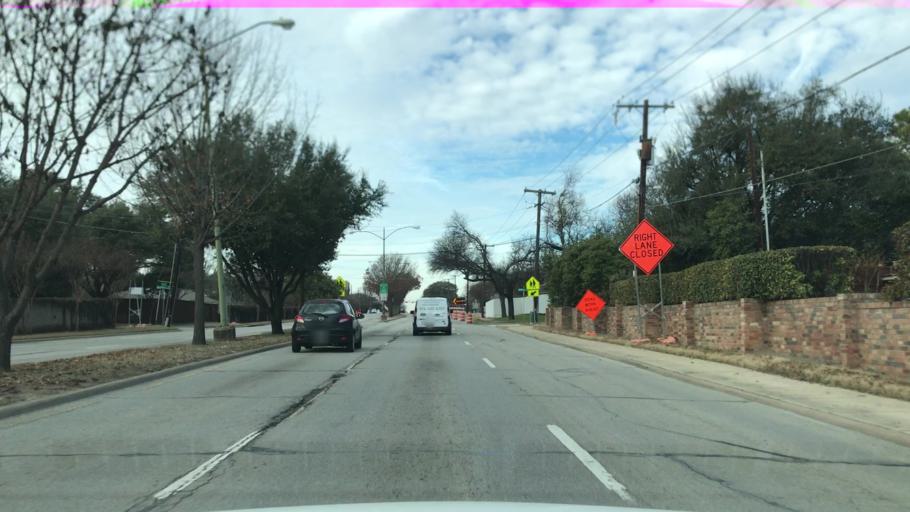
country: US
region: Texas
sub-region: Dallas County
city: University Park
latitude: 32.8801
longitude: -96.7820
